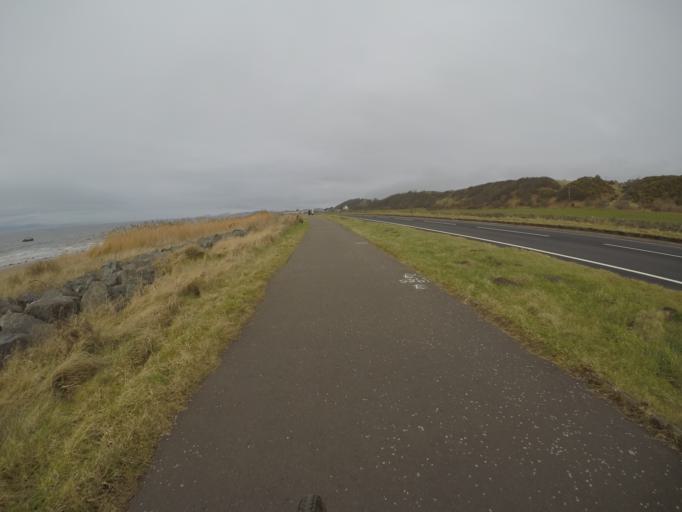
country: GB
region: Scotland
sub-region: North Ayrshire
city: West Kilbride
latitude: 55.6621
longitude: -4.8330
